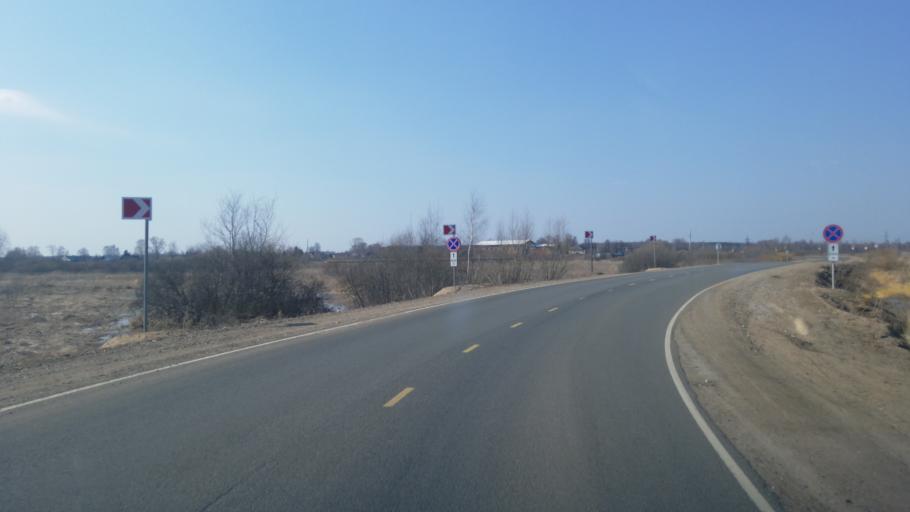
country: RU
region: Jaroslavl
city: Semibratovo
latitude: 57.2297
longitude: 39.5122
